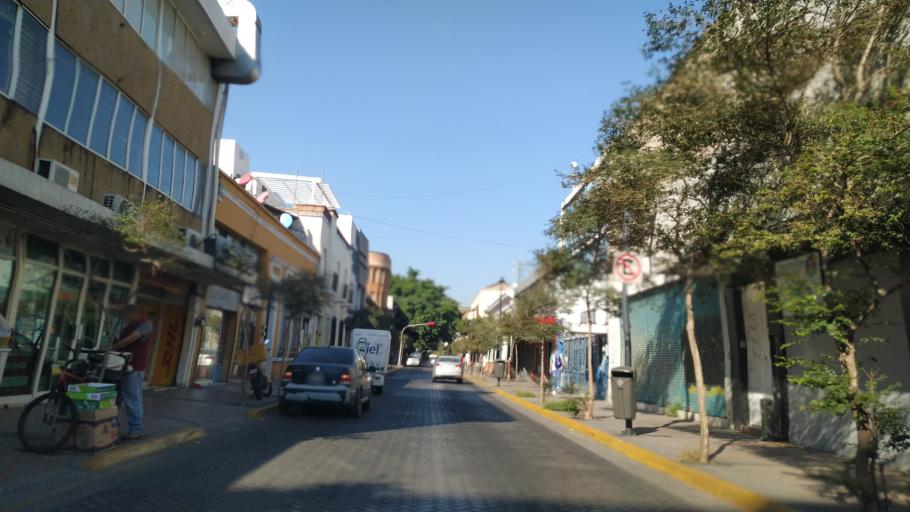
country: MX
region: Jalisco
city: Guadalajara
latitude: 20.6735
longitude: -103.3498
